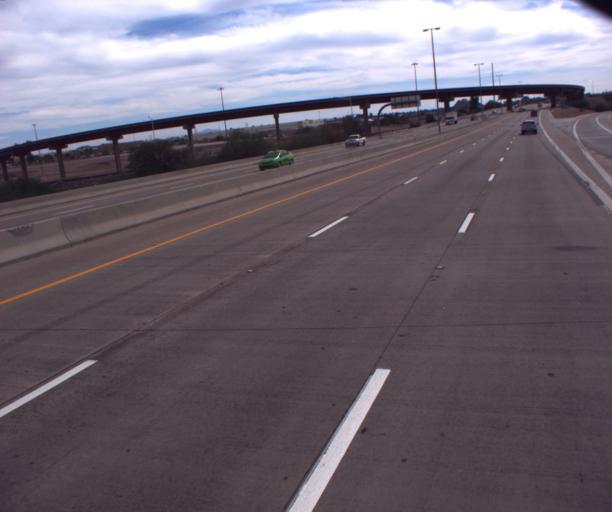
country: US
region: Arizona
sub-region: Maricopa County
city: Tempe Junction
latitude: 33.4400
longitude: -111.9798
